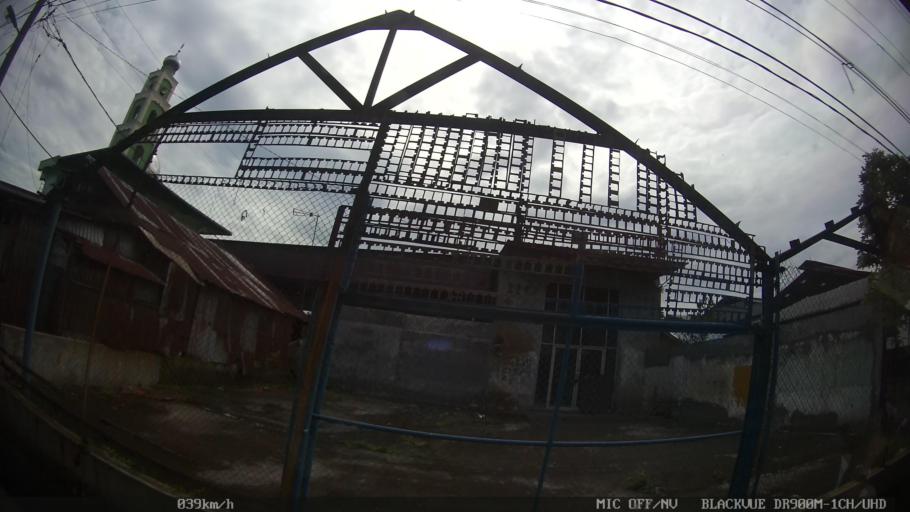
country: ID
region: North Sumatra
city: Sunggal
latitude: 3.5945
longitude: 98.5832
